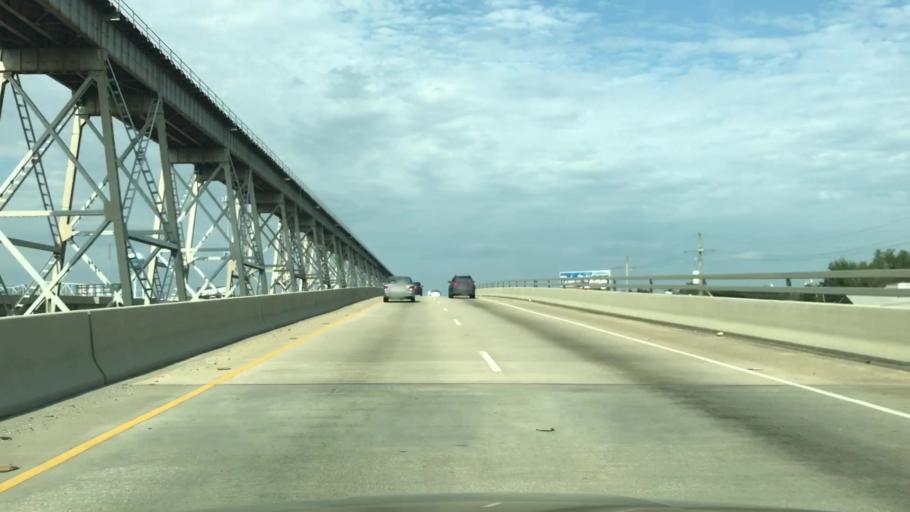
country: US
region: Louisiana
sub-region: Jefferson Parish
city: Bridge City
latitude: 29.9282
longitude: -90.1660
